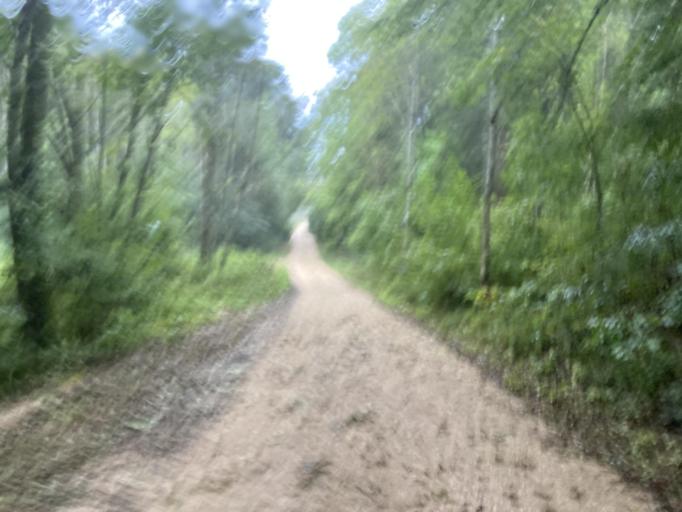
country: DE
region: Baden-Wuerttemberg
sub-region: Tuebingen Region
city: Bingen
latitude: 48.1256
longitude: 9.2592
